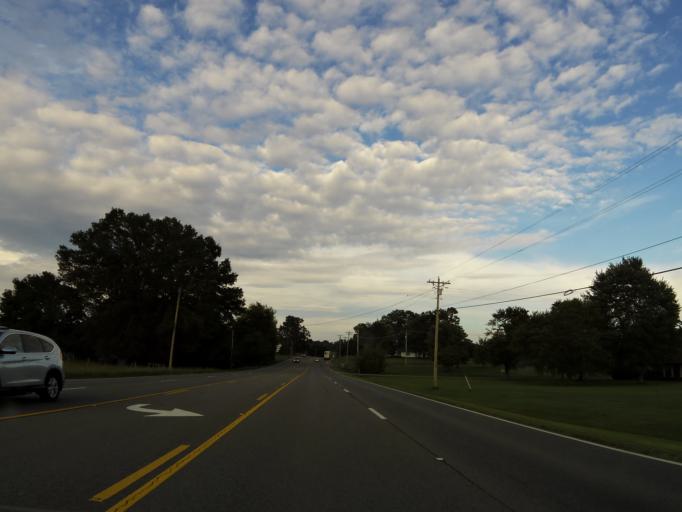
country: US
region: Alabama
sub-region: Lauderdale County
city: Rogersville
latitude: 34.8029
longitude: -87.1984
